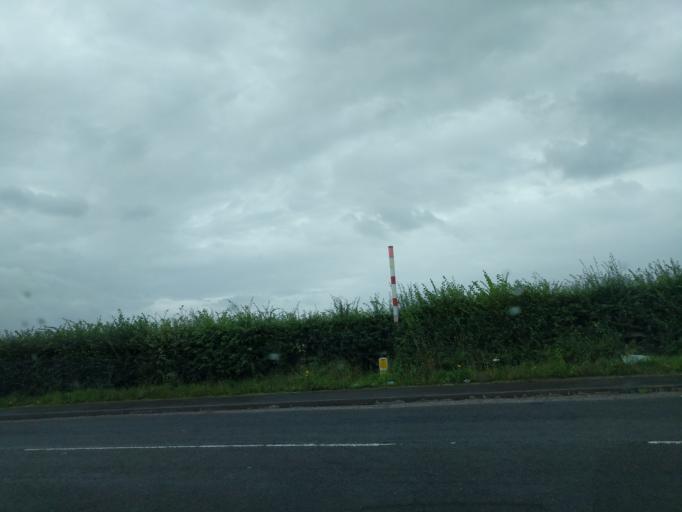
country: GB
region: England
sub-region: Staffordshire
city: Stafford
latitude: 52.8065
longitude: -2.0746
